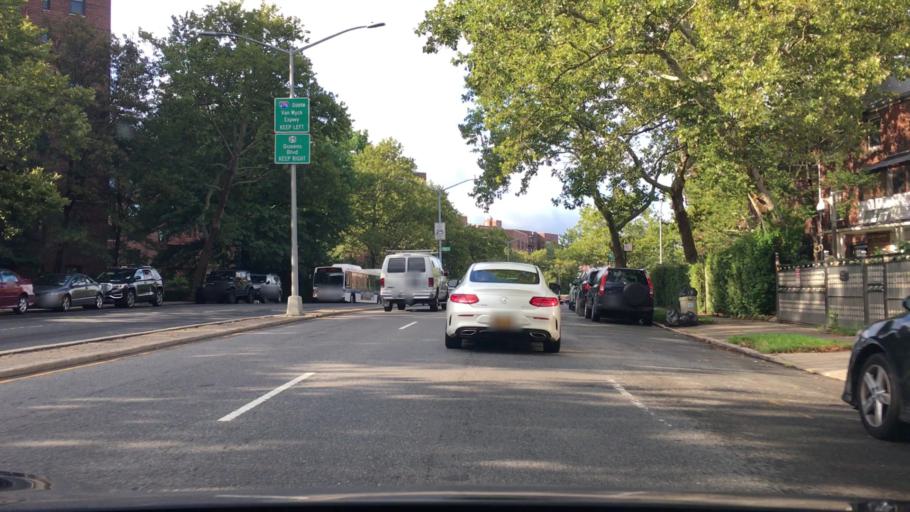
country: US
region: New York
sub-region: Queens County
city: Jamaica
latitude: 40.7141
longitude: -73.8166
